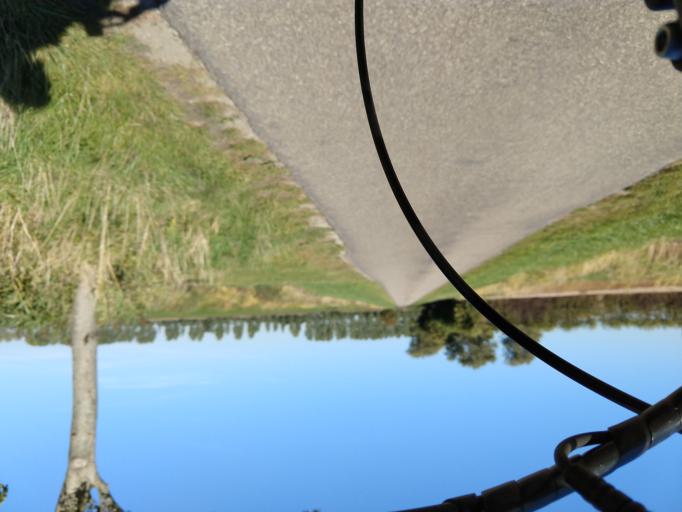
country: NL
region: Zeeland
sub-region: Gemeente Terneuzen
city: Terneuzen
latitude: 51.4005
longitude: 3.8265
